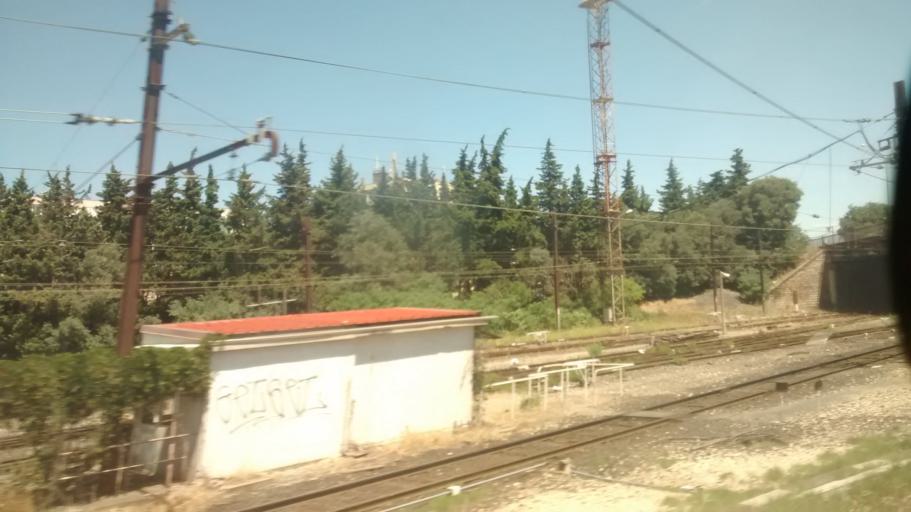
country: FR
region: Languedoc-Roussillon
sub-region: Departement du Gard
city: Rodilhan
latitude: 43.8482
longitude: 4.3975
